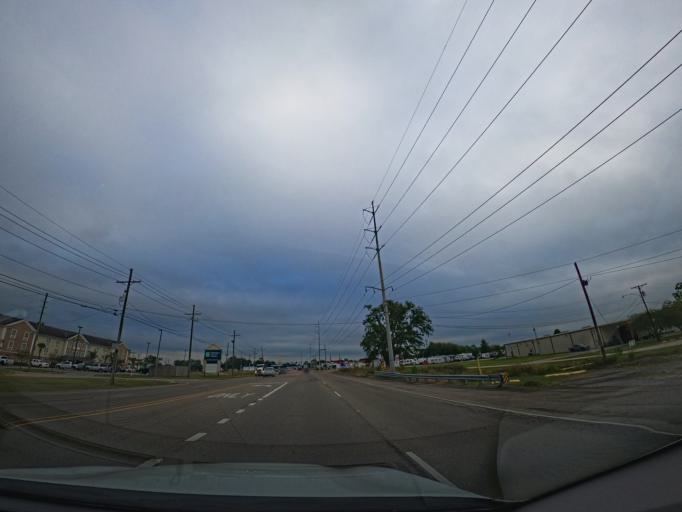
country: US
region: Louisiana
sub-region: Terrebonne Parish
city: Presquille
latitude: 29.5684
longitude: -90.6826
